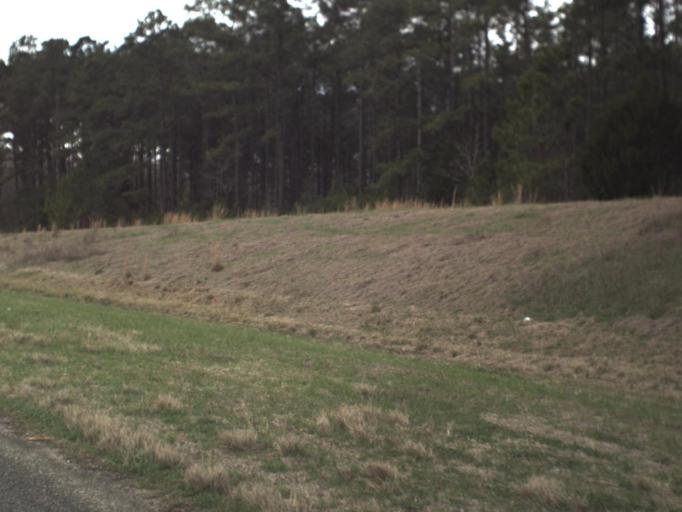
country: US
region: Florida
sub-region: Jackson County
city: Marianna
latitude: 30.8268
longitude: -85.3601
